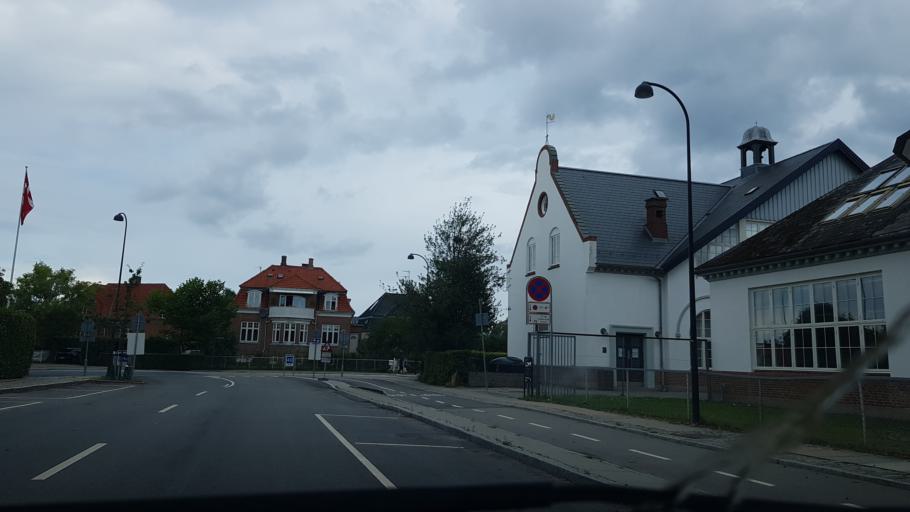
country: DK
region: Capital Region
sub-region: Gentofte Kommune
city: Charlottenlund
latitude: 55.7620
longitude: 12.5935
